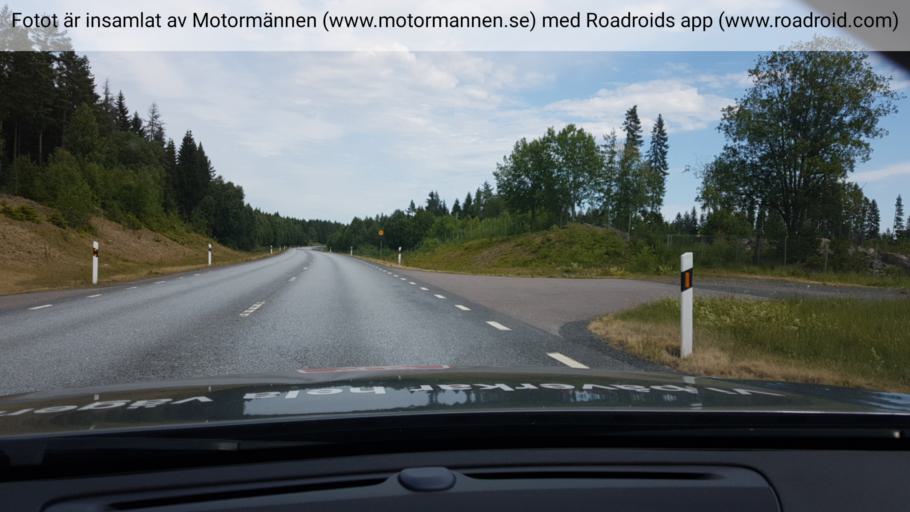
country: SE
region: Uppsala
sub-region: Osthammars Kommun
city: Gimo
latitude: 60.1688
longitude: 18.2847
